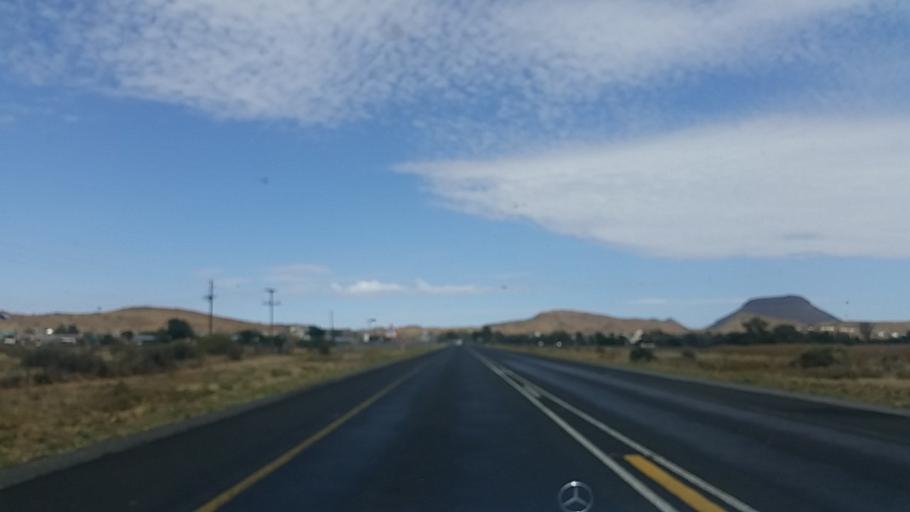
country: ZA
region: Northern Cape
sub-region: Pixley ka Seme District Municipality
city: Colesberg
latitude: -30.7047
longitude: 25.1163
